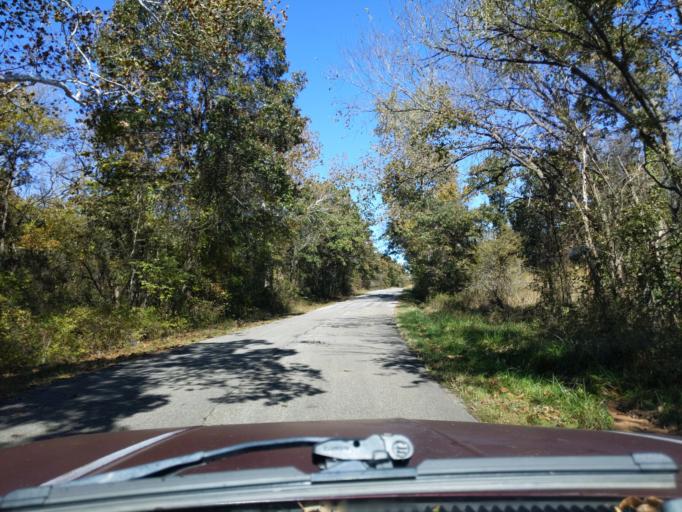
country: US
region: Oklahoma
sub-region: Creek County
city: Bristow
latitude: 35.7070
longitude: -96.4053
